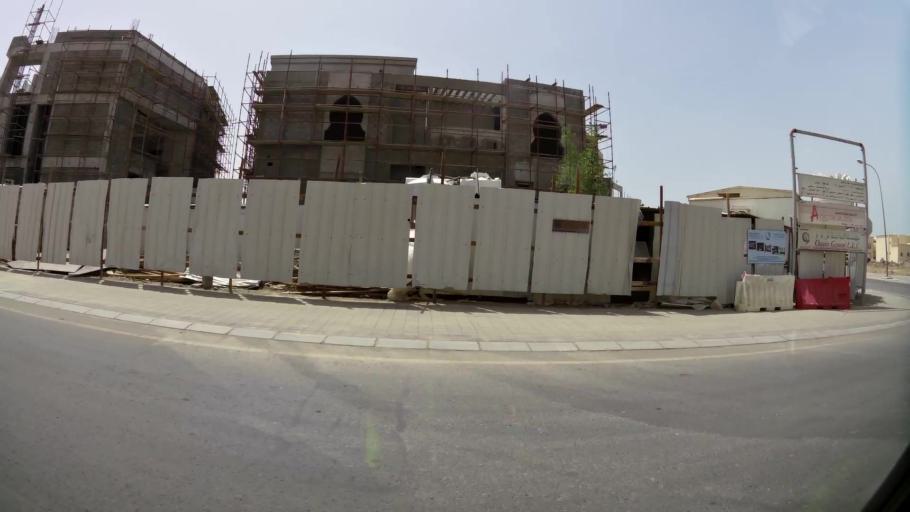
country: OM
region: Muhafazat Masqat
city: Bawshar
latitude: 23.5624
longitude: 58.3979
